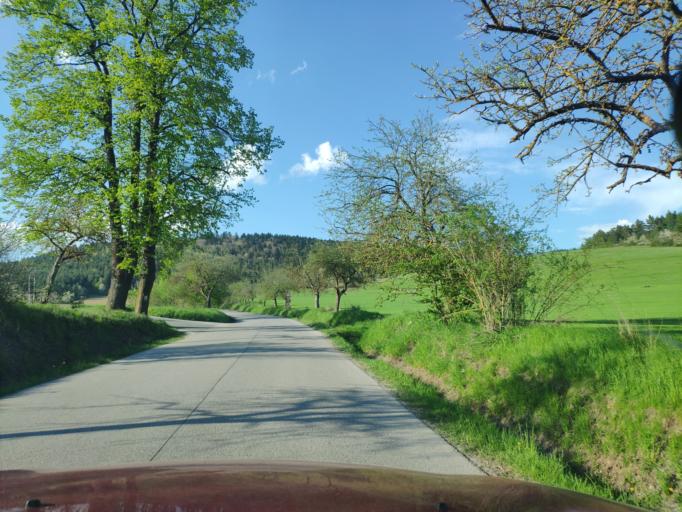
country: SK
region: Presovsky
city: Spisske Podhradie
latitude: 49.0282
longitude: 20.7973
